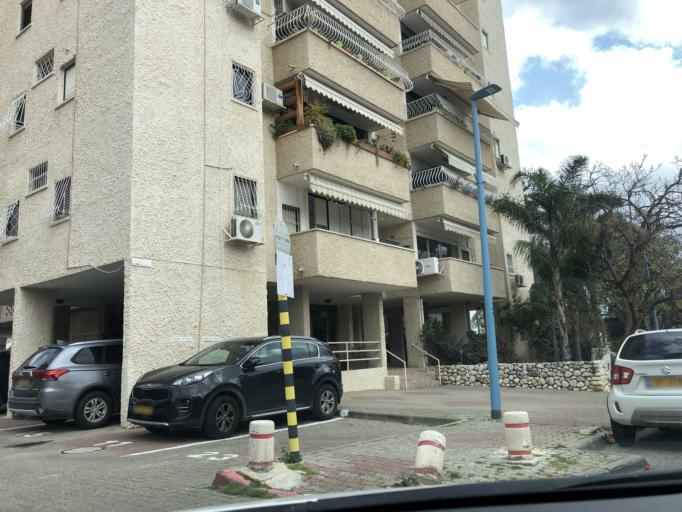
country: IL
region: Central District
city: Ganne Tiqwa
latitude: 32.0571
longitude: 34.8669
